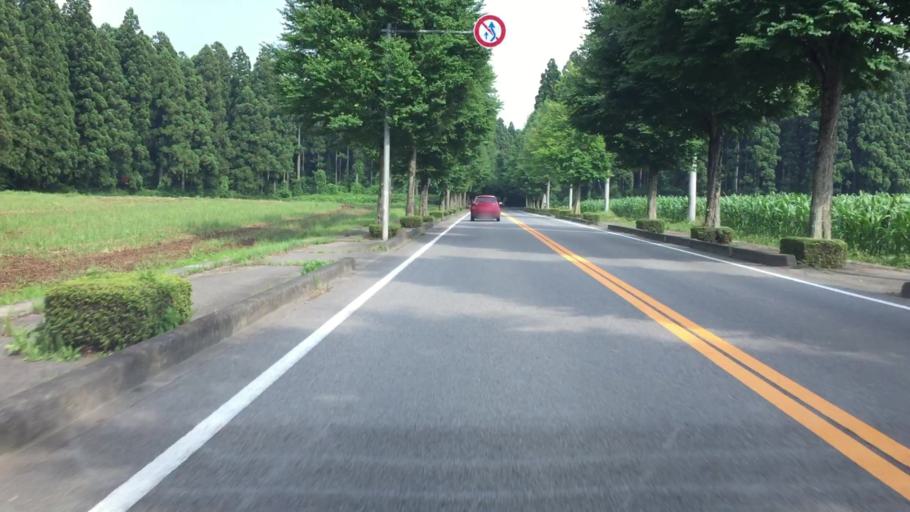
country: JP
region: Tochigi
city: Kuroiso
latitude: 36.9783
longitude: 139.9660
